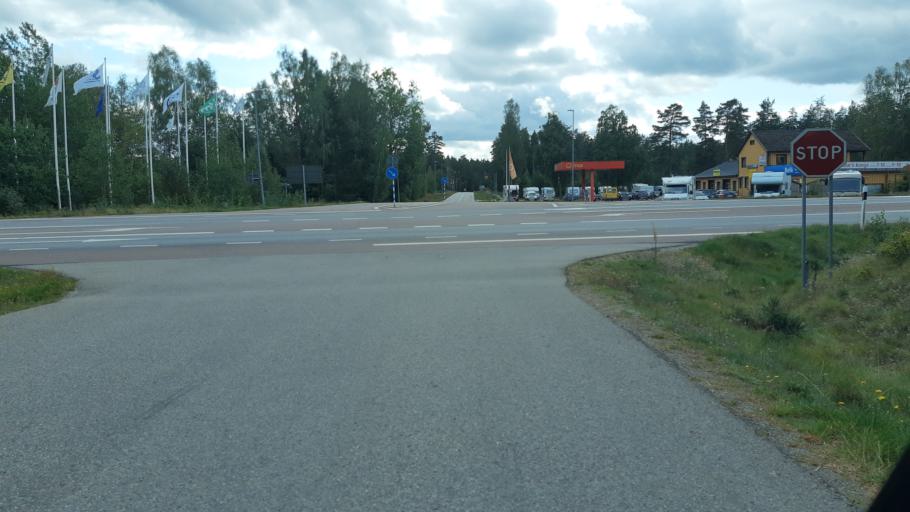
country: SE
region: Kronoberg
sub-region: Tingsryds Kommun
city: Tingsryd
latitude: 56.5059
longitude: 15.1287
